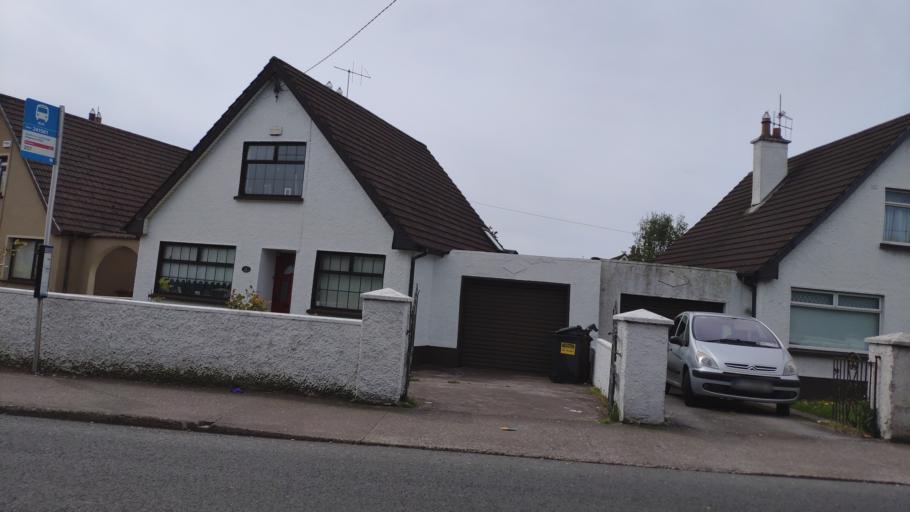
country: IE
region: Munster
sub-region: County Cork
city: Cork
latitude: 51.9181
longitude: -8.4482
